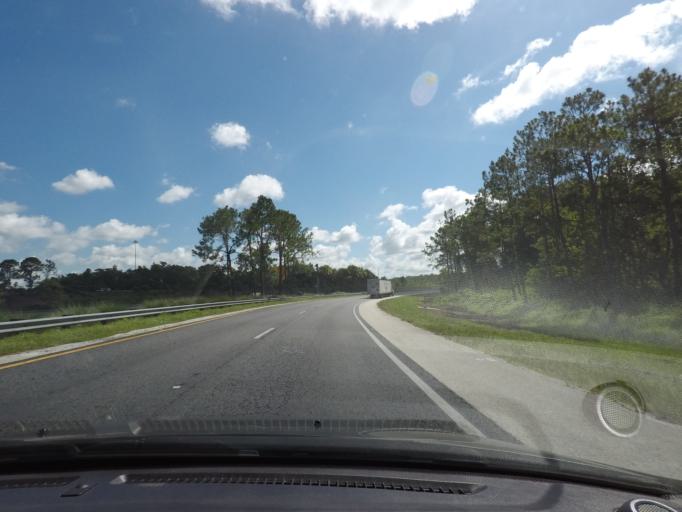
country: US
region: Florida
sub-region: Orange County
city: Alafaya
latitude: 28.4505
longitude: -81.2267
